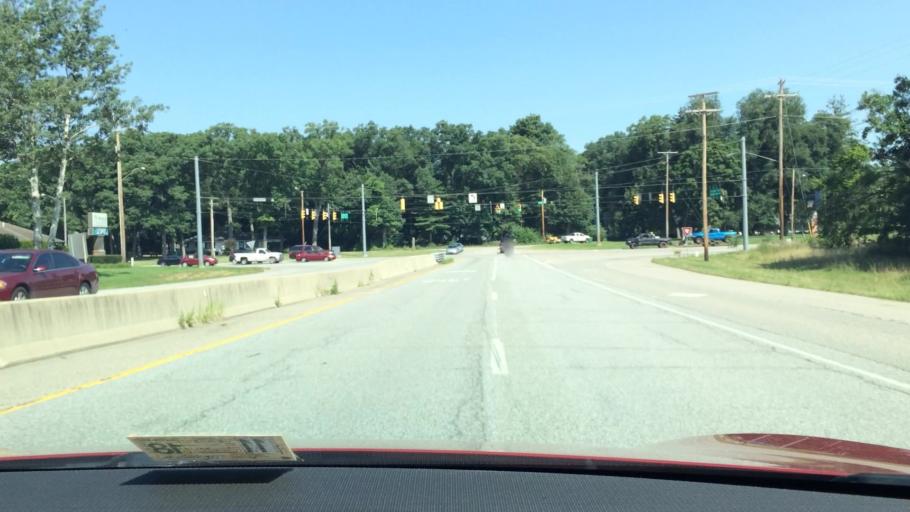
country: US
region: Indiana
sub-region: Saint Joseph County
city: Granger
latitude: 41.7358
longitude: -86.1513
